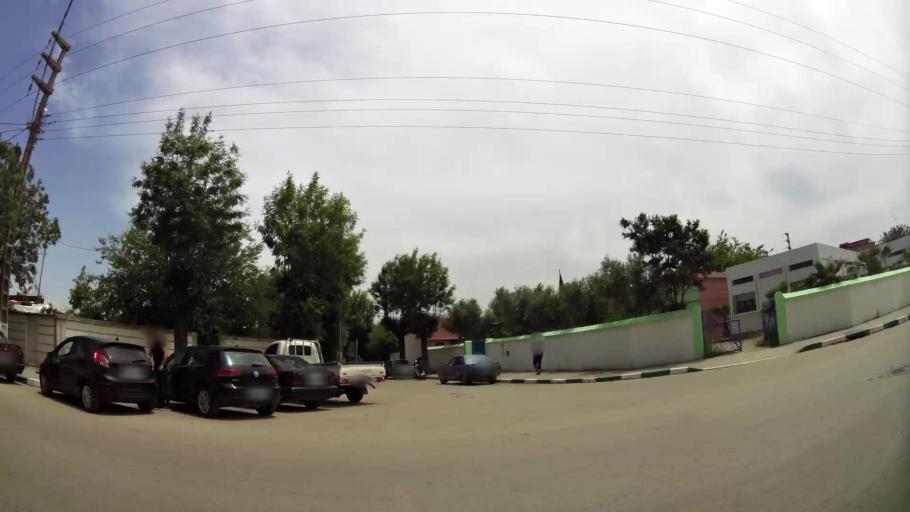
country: MA
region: Rabat-Sale-Zemmour-Zaer
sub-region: Khemisset
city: Khemisset
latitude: 33.8231
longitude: -6.0652
